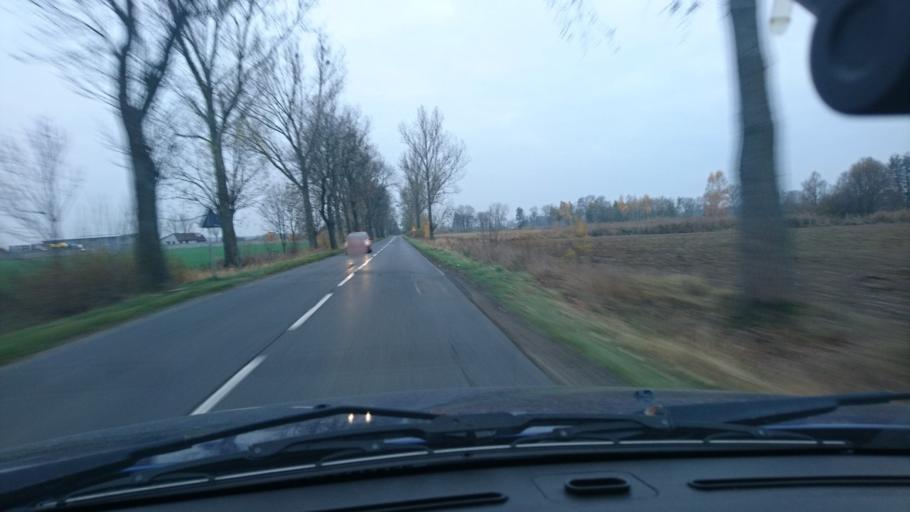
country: PL
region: Greater Poland Voivodeship
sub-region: Powiat ostrowski
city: Odolanow
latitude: 51.5615
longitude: 17.6618
